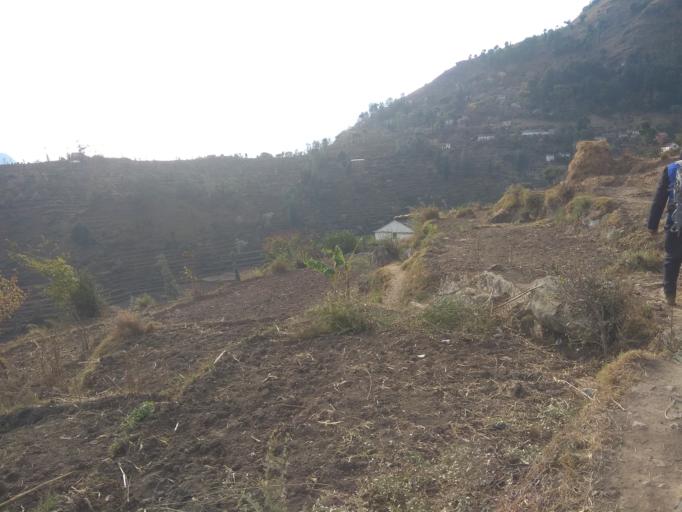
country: NP
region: Mid Western
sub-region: Bheri Zone
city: Dailekh
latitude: 29.2512
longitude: 81.6662
